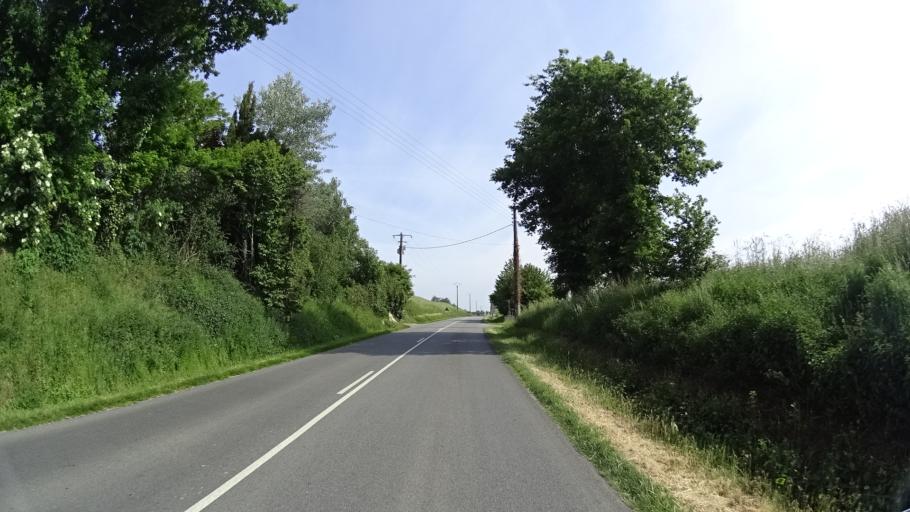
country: FR
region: Brittany
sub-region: Departement d'Ille-et-Vilaine
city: Chateaugiron
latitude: 48.0263
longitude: -1.5061
